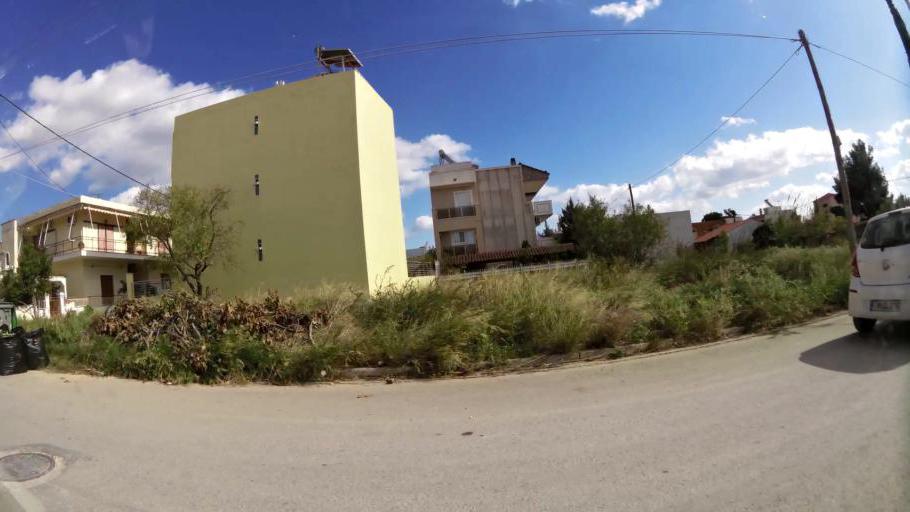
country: GR
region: Attica
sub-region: Nomarchia Anatolikis Attikis
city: Acharnes
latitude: 38.1010
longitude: 23.7473
